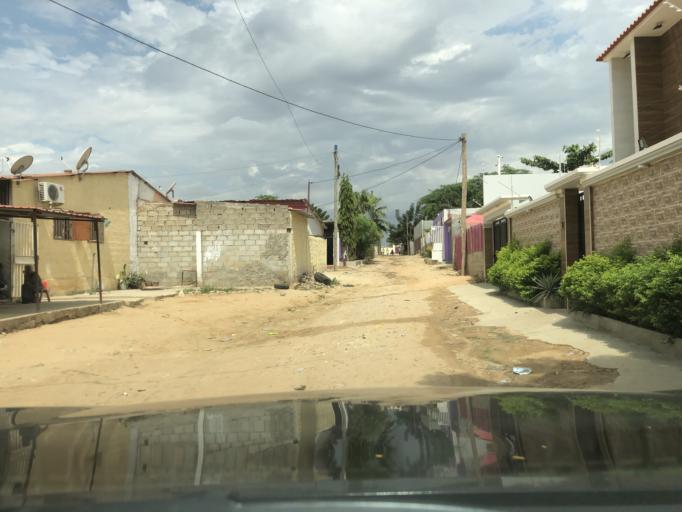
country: AO
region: Luanda
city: Luanda
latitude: -8.9394
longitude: 13.2519
